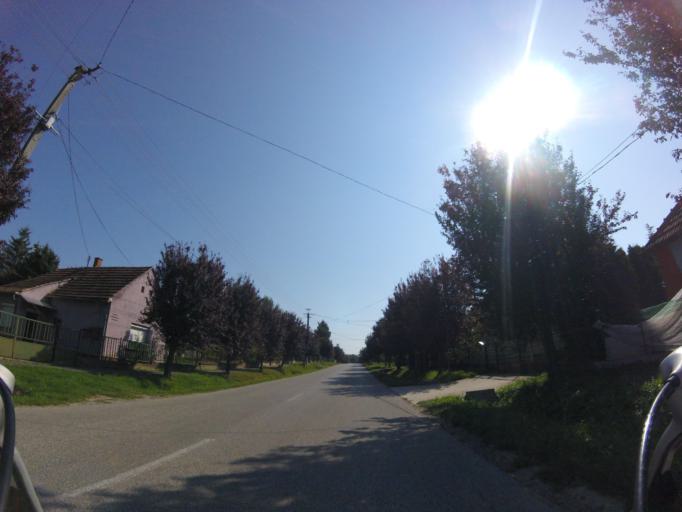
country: HU
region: Zala
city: Zalakomar
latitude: 46.5260
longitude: 17.1803
